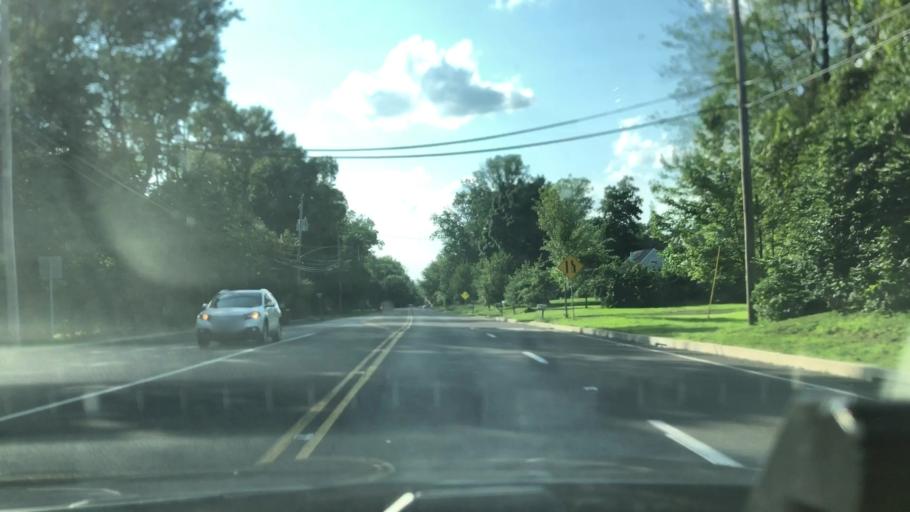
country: US
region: Pennsylvania
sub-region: Bucks County
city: Brittany Farms-Highlands
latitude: 40.2669
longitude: -75.2303
